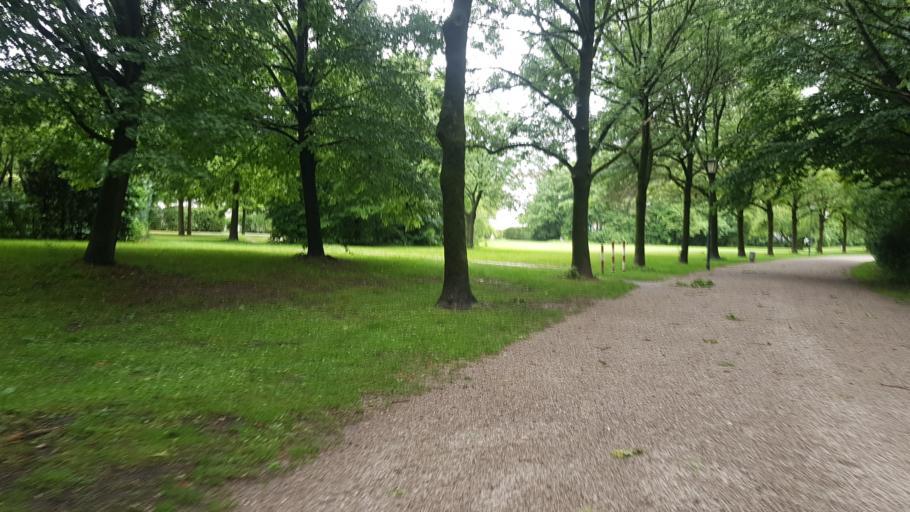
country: DE
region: Bavaria
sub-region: Upper Bavaria
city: Unterfoehring
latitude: 48.2039
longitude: 11.6041
